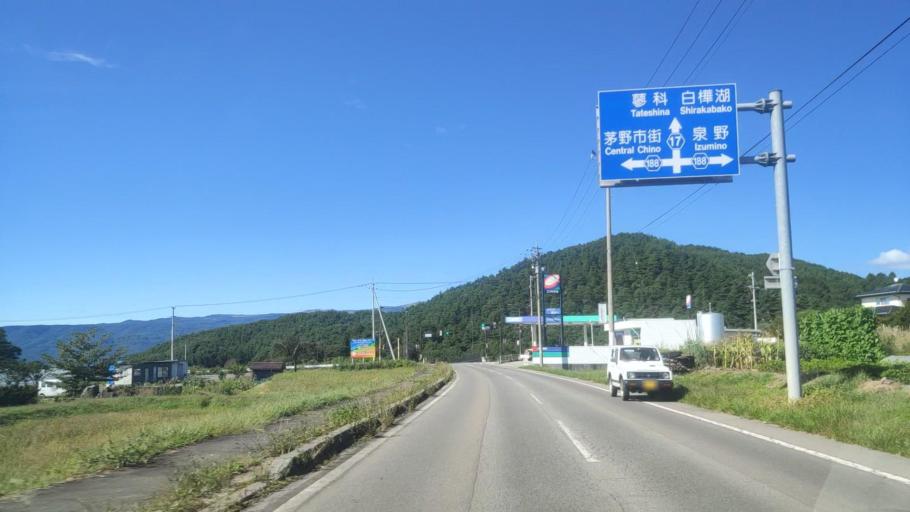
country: JP
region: Nagano
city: Chino
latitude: 35.9915
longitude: 138.2159
